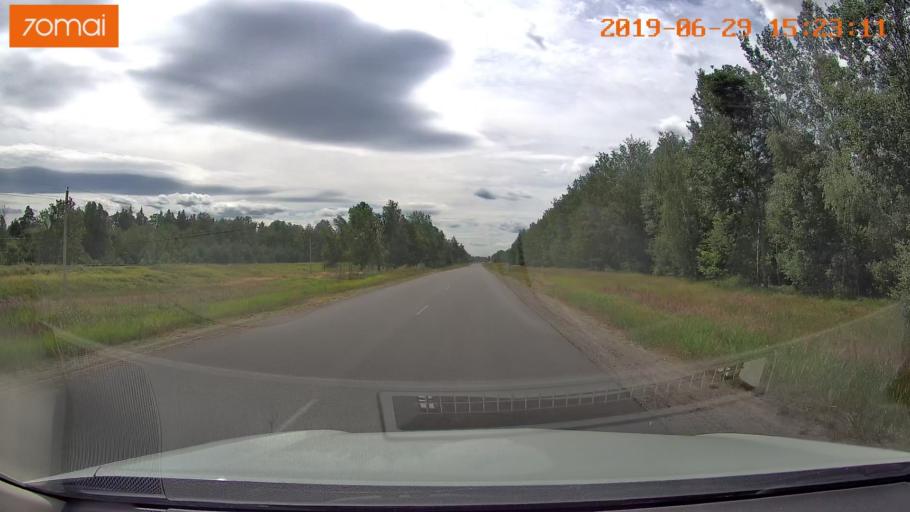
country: BY
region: Brest
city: Mikashevichy
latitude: 52.2118
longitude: 27.4370
